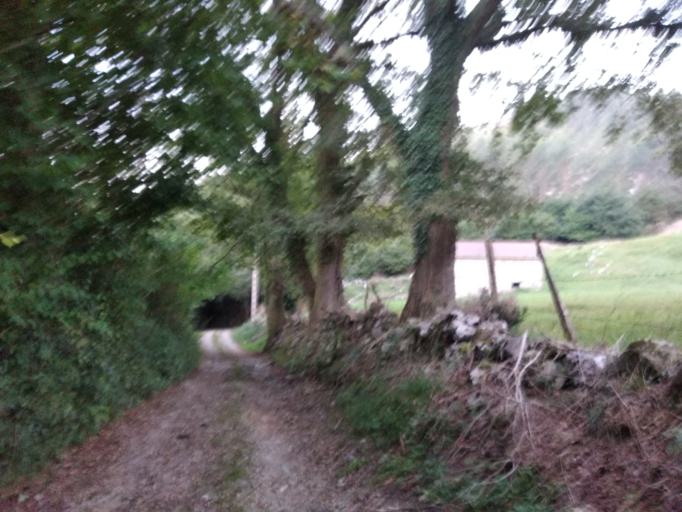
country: ES
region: Cantabria
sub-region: Provincia de Cantabria
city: Entrambasaguas
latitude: 43.3321
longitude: -3.6813
